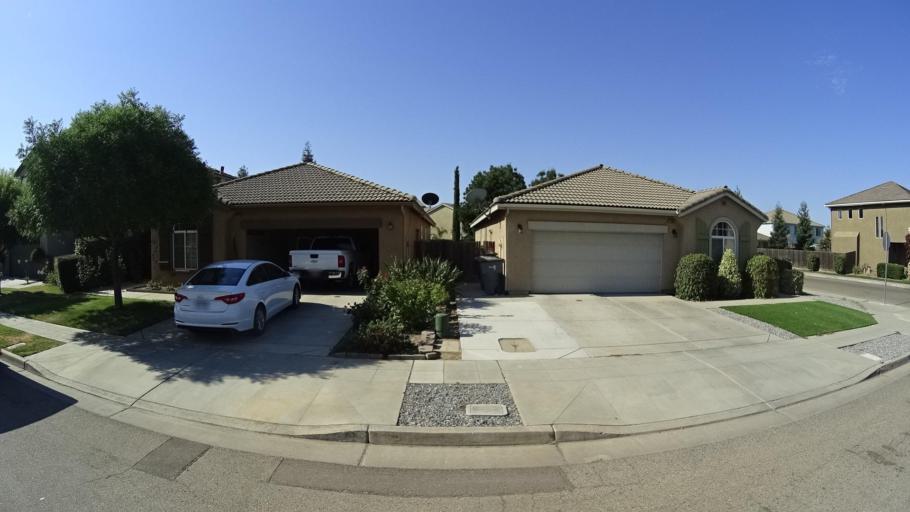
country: US
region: California
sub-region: Fresno County
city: Tarpey Village
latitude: 36.7816
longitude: -119.6593
